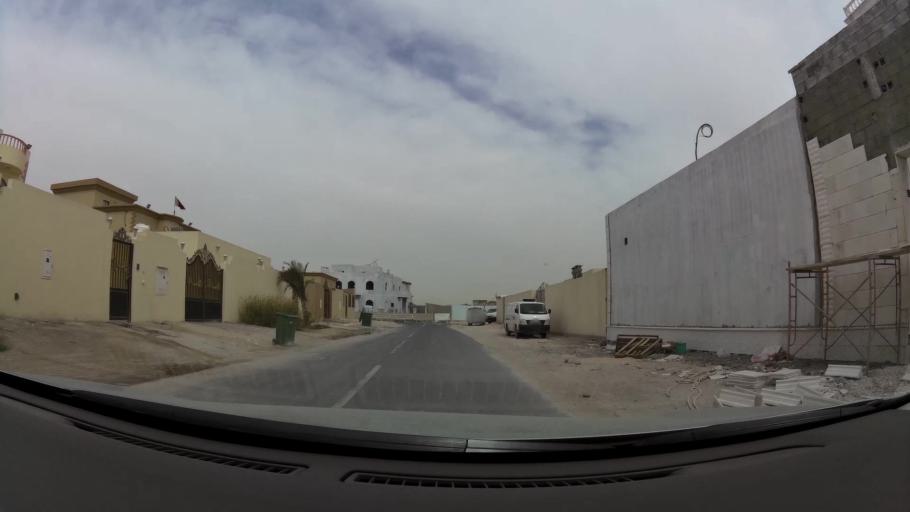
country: QA
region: Al Wakrah
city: Al Wukayr
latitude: 25.1977
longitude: 51.4539
